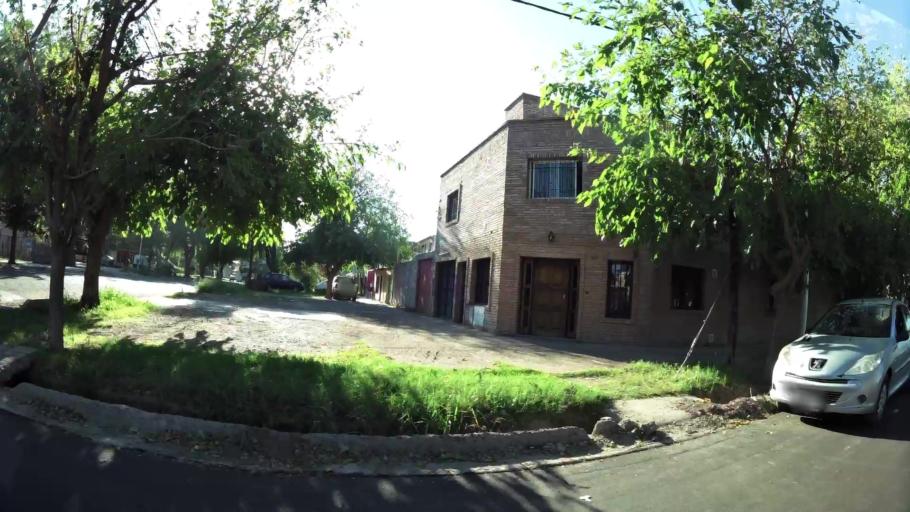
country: AR
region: Mendoza
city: Las Heras
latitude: -32.8549
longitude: -68.8188
